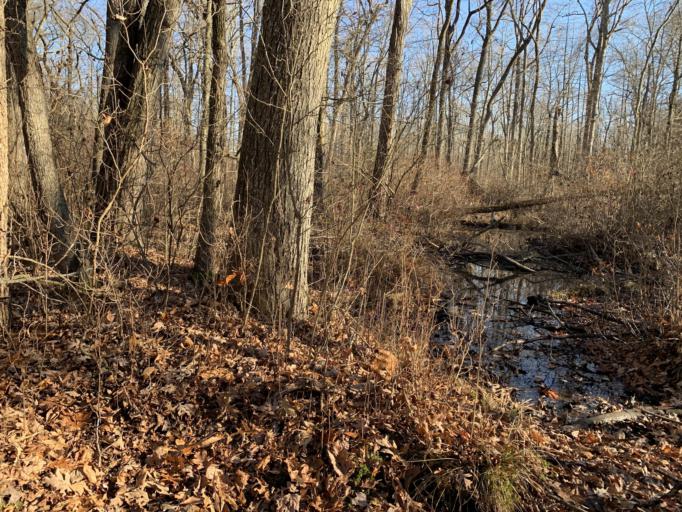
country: US
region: Delaware
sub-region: New Castle County
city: Townsend
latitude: 39.3421
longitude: -75.7385
